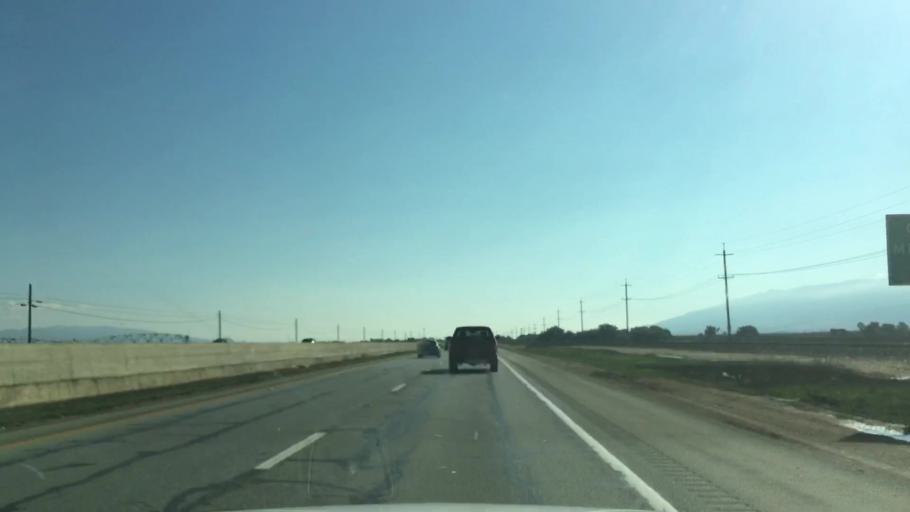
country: US
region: California
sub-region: Monterey County
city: Chualar
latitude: 36.5877
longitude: -121.5376
